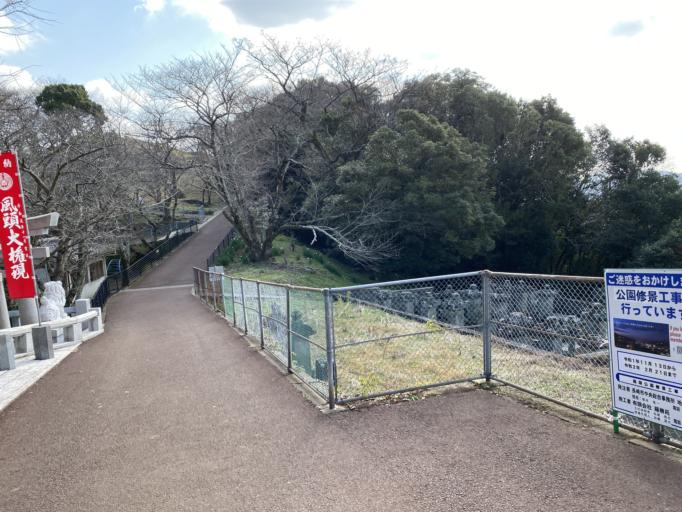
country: JP
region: Nagasaki
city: Nagasaki-shi
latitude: 32.7456
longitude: 129.8862
